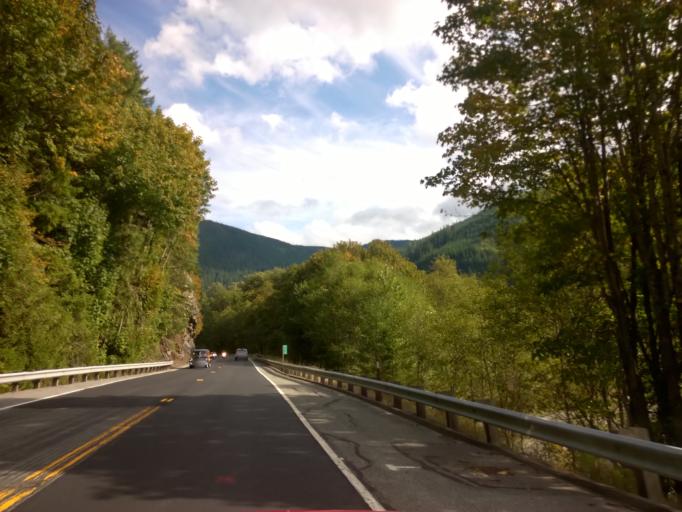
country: US
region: Washington
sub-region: Snohomish County
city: Gold Bar
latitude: 47.7160
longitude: -121.2731
